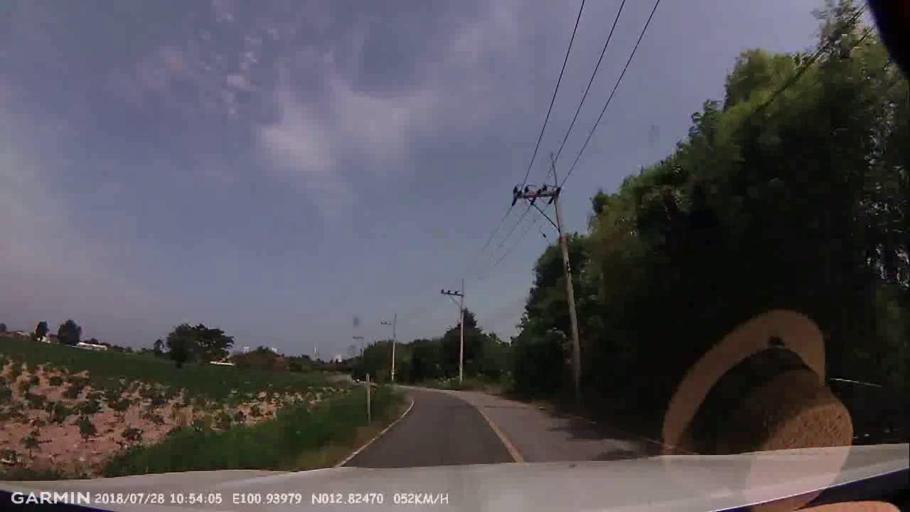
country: TH
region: Chon Buri
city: Phatthaya
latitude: 12.8248
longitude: 100.9397
